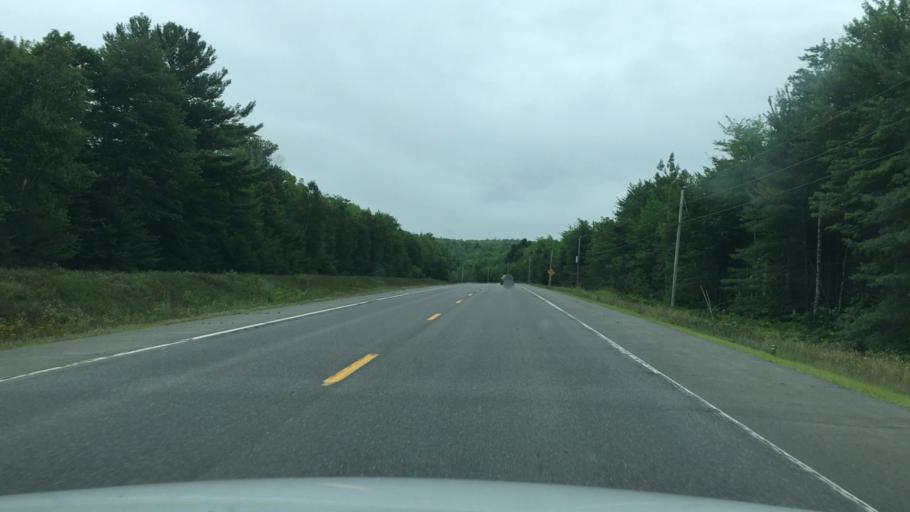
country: US
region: Maine
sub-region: Hancock County
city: Franklin
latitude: 44.8332
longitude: -68.1374
